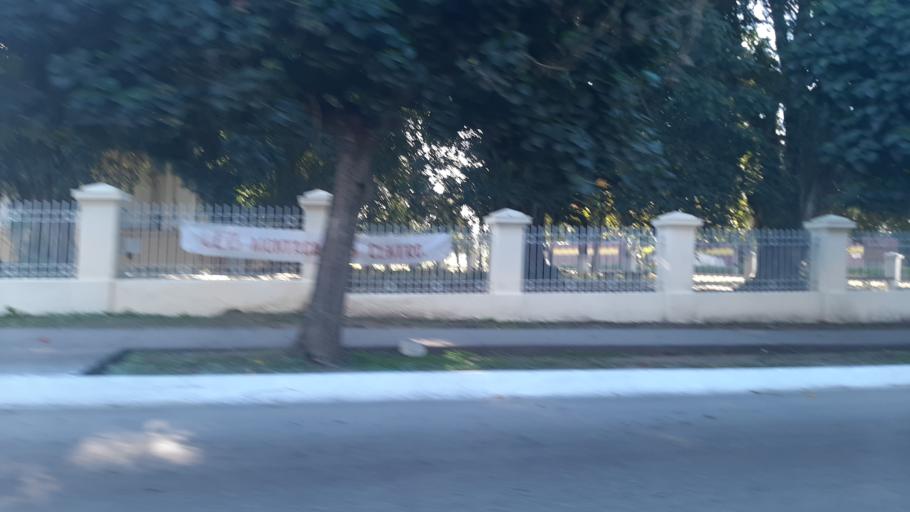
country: CU
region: Villa Clara
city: Santa Clara
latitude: 22.4105
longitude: -79.9599
